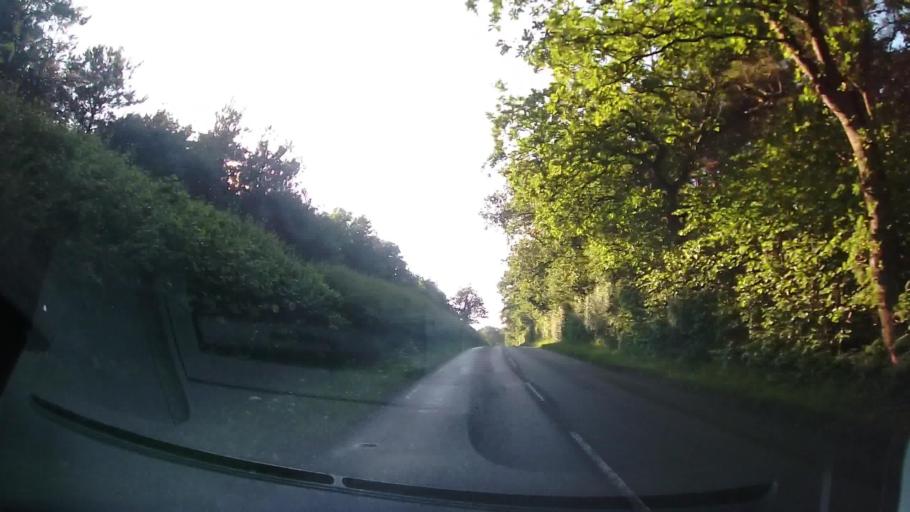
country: GB
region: England
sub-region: Leicestershire
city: Markfield
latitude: 52.6553
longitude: -1.2570
